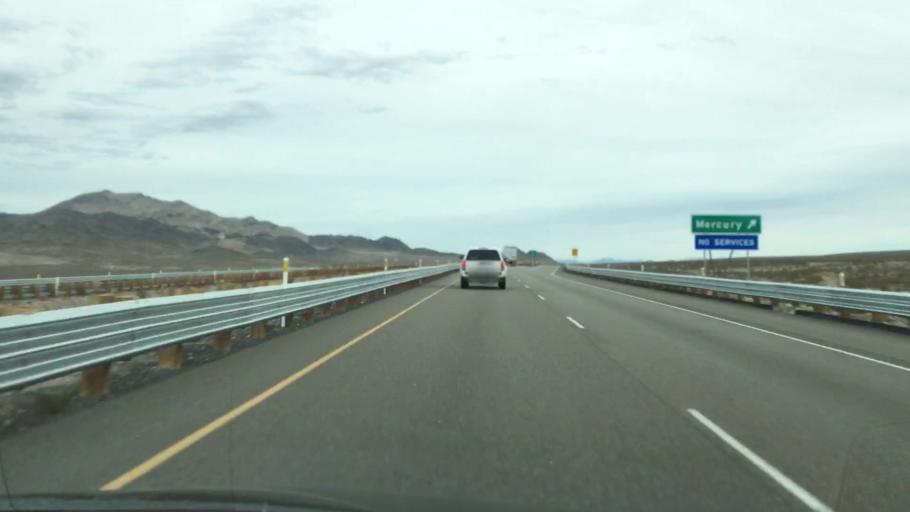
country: US
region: Nevada
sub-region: Nye County
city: Pahrump
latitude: 36.5972
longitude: -116.0023
